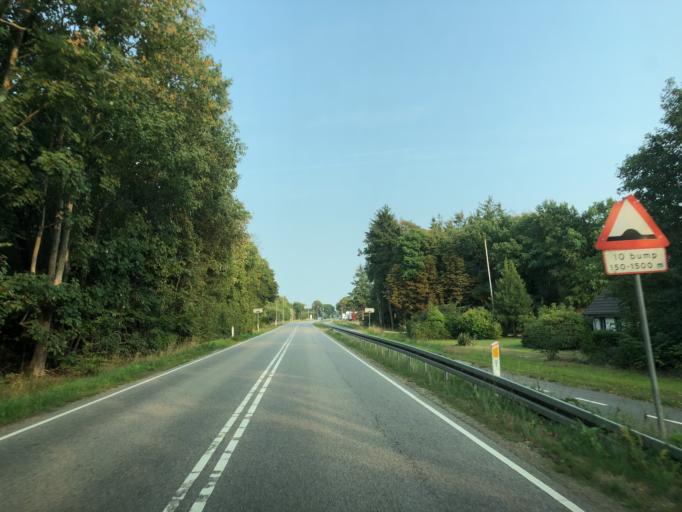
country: DK
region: South Denmark
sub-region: Billund Kommune
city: Grindsted
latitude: 55.8170
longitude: 9.0154
